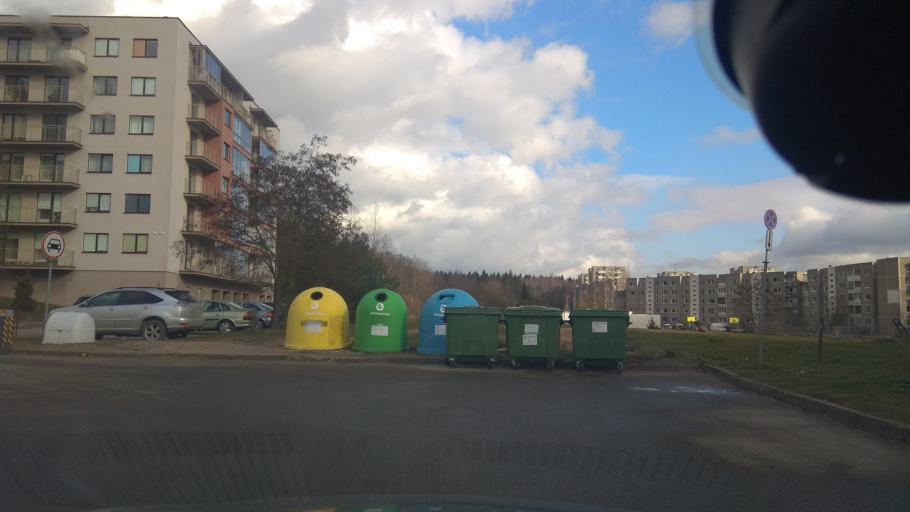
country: LT
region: Vilnius County
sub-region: Vilnius
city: Fabijoniskes
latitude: 54.7401
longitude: 25.2340
